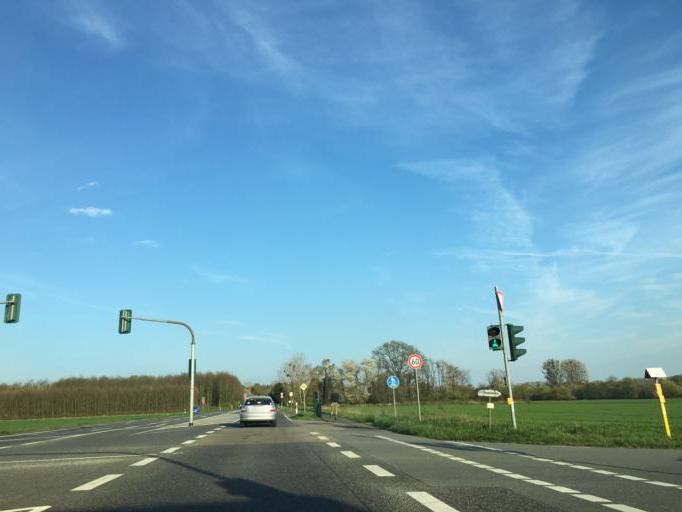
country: DE
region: Hesse
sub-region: Regierungsbezirk Darmstadt
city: Maintal
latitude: 50.1372
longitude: 8.8024
